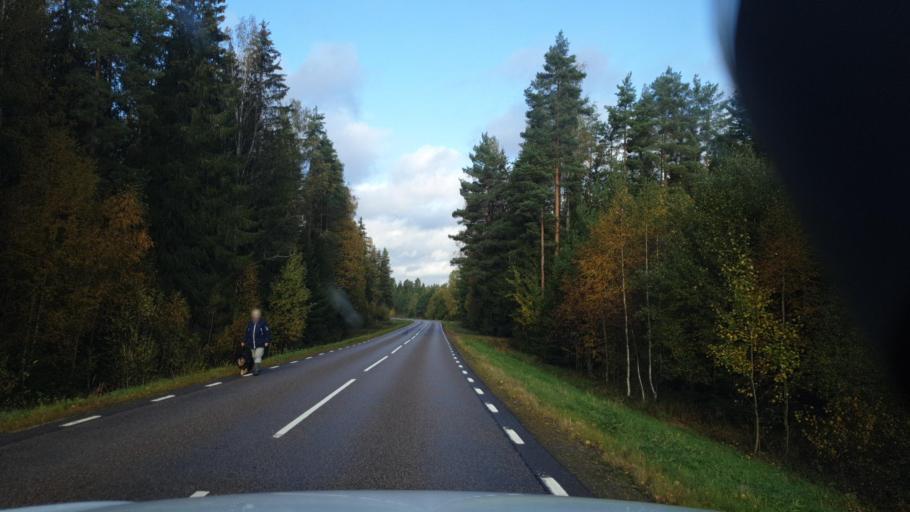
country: SE
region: Vaermland
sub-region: Arvika Kommun
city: Arvika
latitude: 59.5153
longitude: 12.6346
